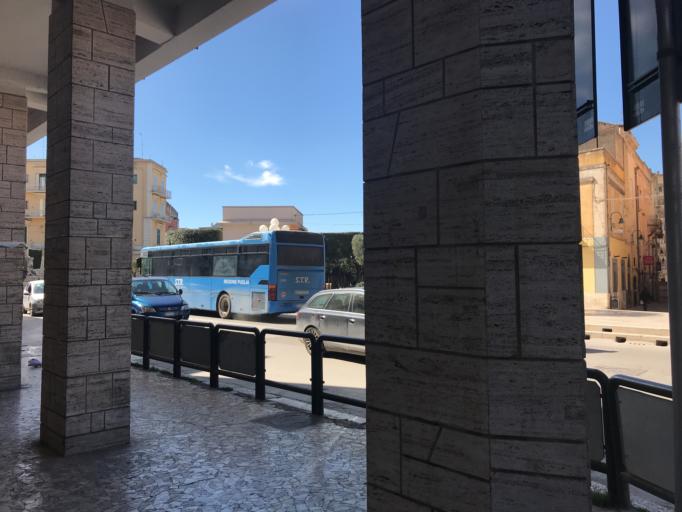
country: IT
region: Apulia
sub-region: Provincia di Bari
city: Gravina in Puglia
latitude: 40.8172
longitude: 16.4186
